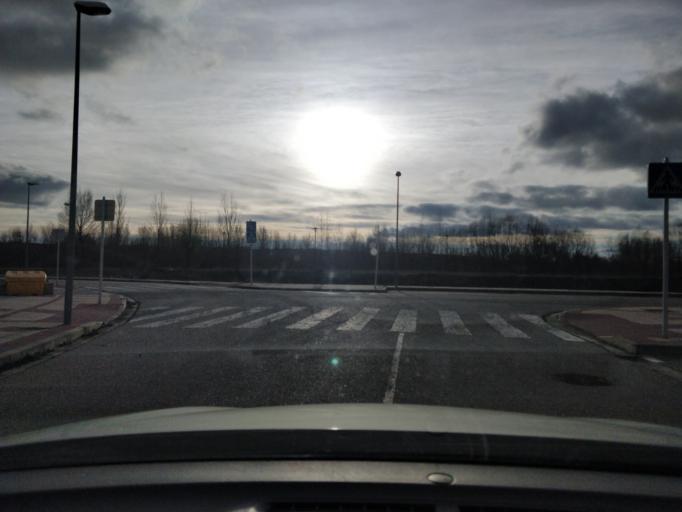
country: ES
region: Castille and Leon
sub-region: Provincia de Burgos
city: Villalbilla de Burgos
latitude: 42.3525
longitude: -3.7581
